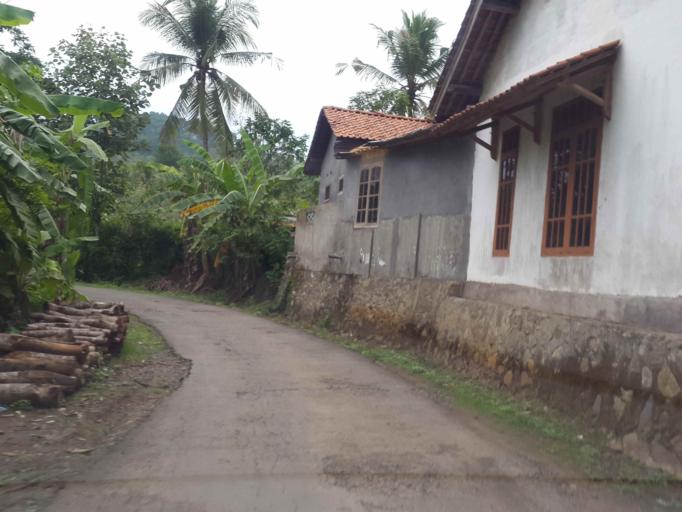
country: ID
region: Central Java
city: Pasanggrahan
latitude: -7.3696
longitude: 108.8986
